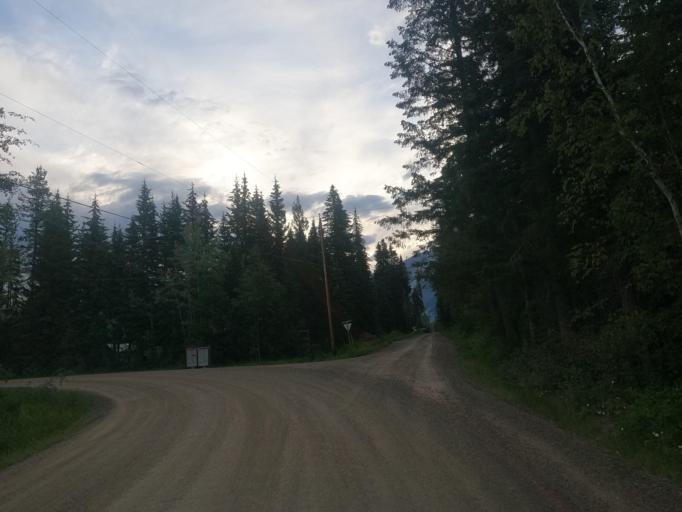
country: CA
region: British Columbia
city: Golden
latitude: 51.4384
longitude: -117.0417
